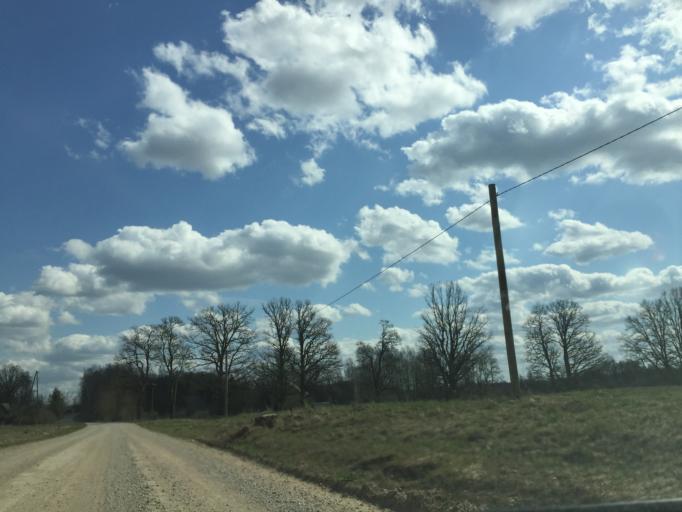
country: LV
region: Skriveri
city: Skriveri
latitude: 56.7547
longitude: 25.0705
